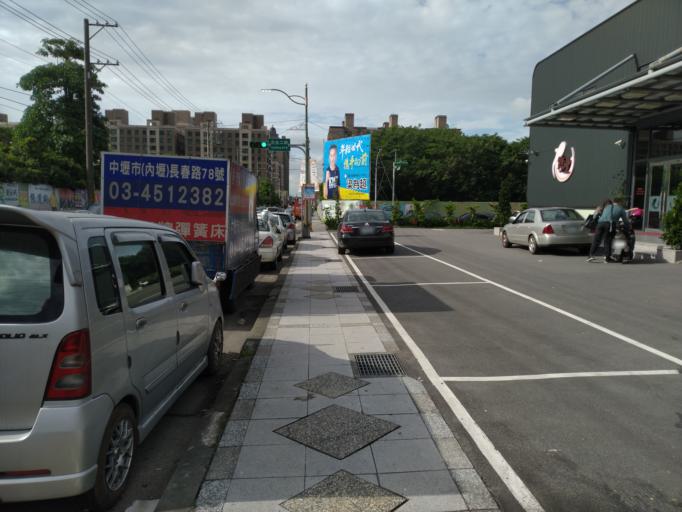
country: TW
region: Taiwan
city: Taoyuan City
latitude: 24.9756
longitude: 121.2530
